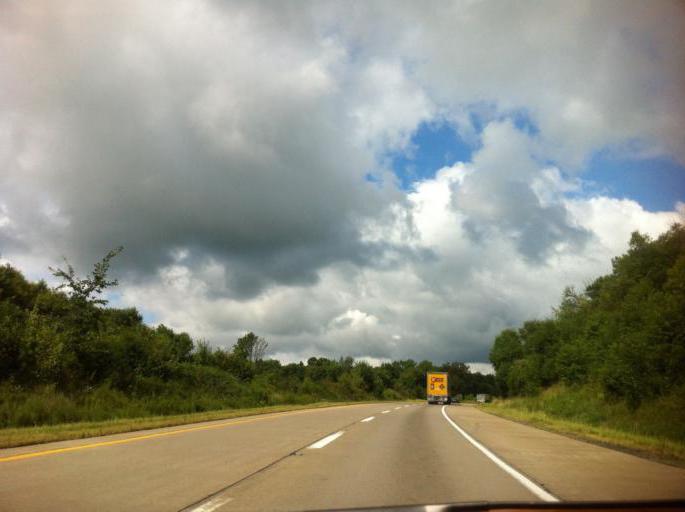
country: US
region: Pennsylvania
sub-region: Lawrence County
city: New Wilmington
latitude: 41.1810
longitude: -80.3110
